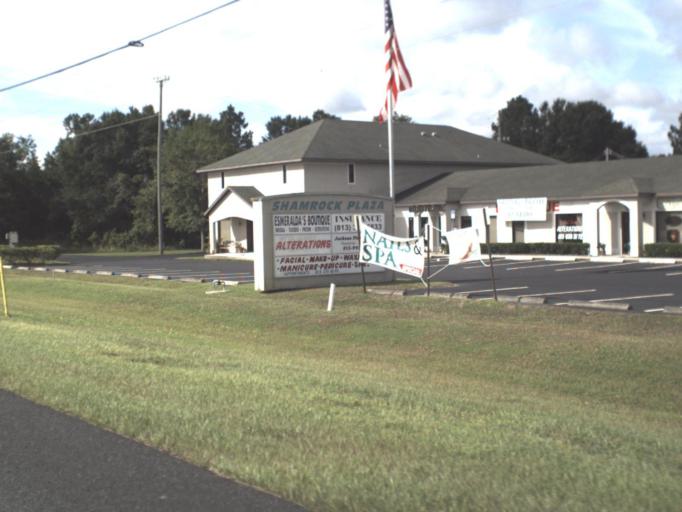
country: US
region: Florida
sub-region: Pasco County
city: Land O' Lakes
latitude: 28.2591
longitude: -82.4745
